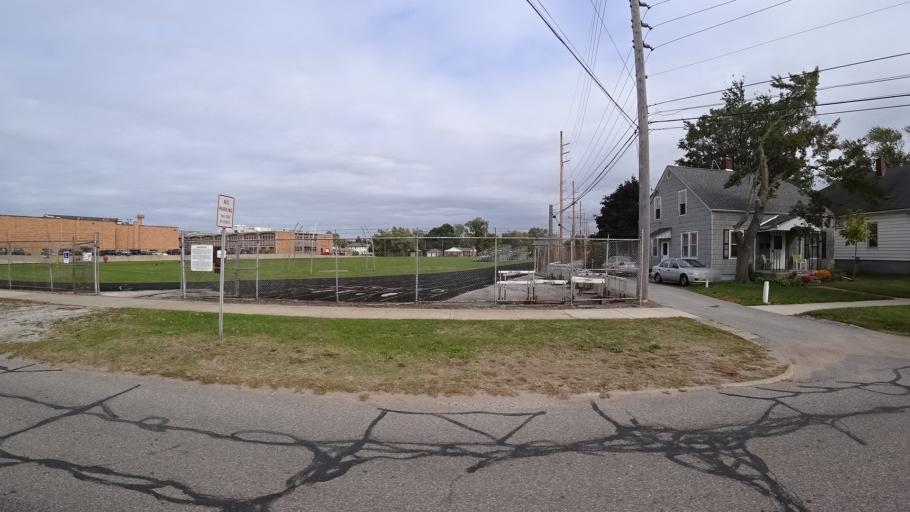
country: US
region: Indiana
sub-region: LaPorte County
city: Michigan City
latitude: 41.7080
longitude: -86.8955
